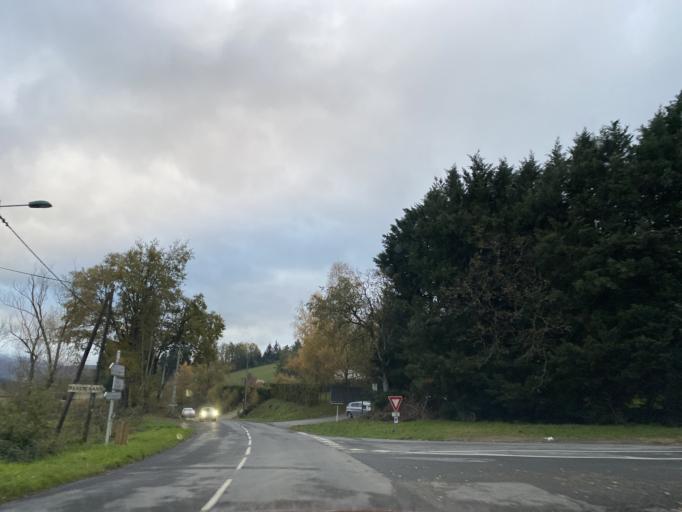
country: FR
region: Auvergne
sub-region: Departement du Puy-de-Dome
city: Courpiere
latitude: 45.7191
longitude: 3.6181
